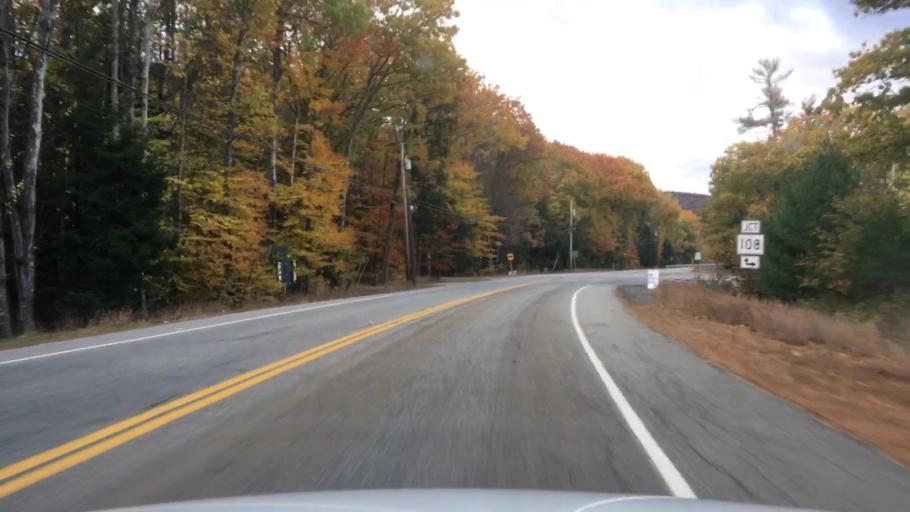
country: US
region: Maine
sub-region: Androscoggin County
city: Livermore
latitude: 44.3870
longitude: -70.2564
